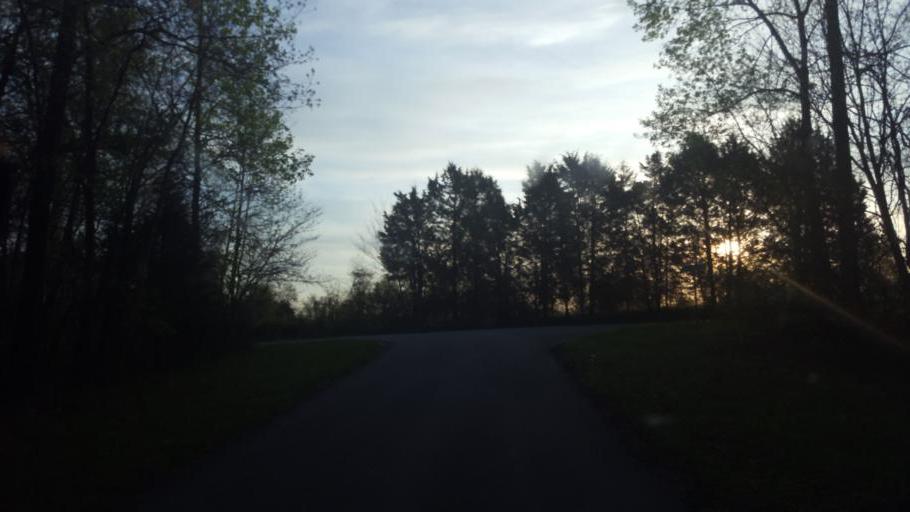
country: US
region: Kentucky
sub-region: Barren County
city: Cave City
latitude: 37.1701
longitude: -86.0043
